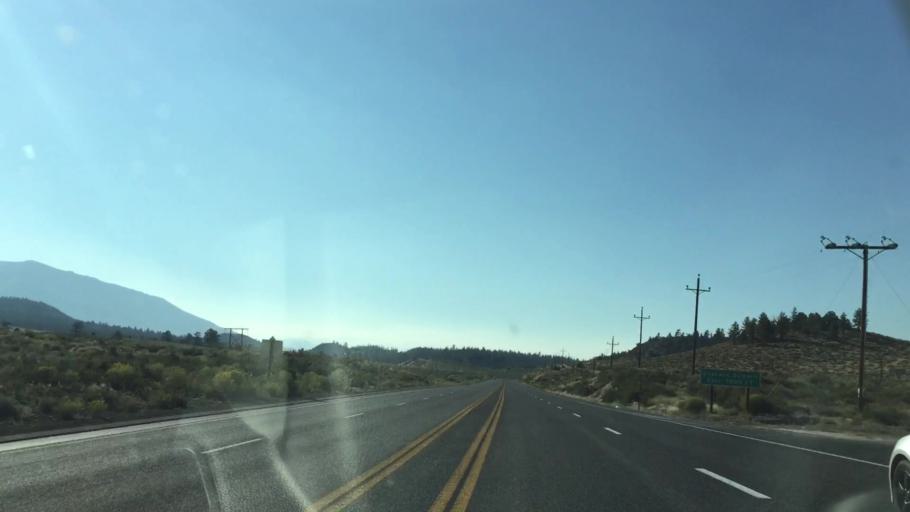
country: US
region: California
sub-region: Inyo County
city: West Bishop
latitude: 37.5517
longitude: -118.6416
